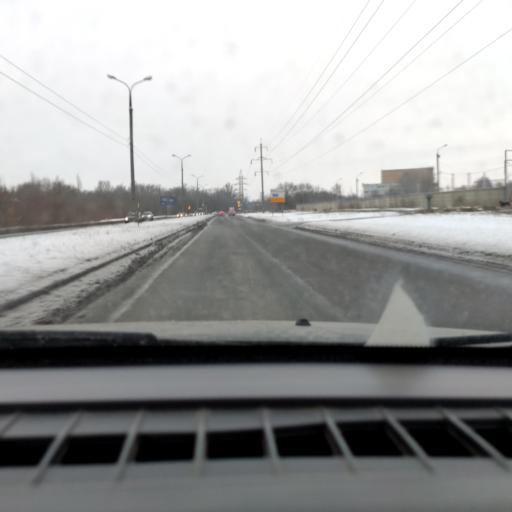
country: RU
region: Samara
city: Tol'yatti
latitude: 53.5563
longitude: 49.3193
